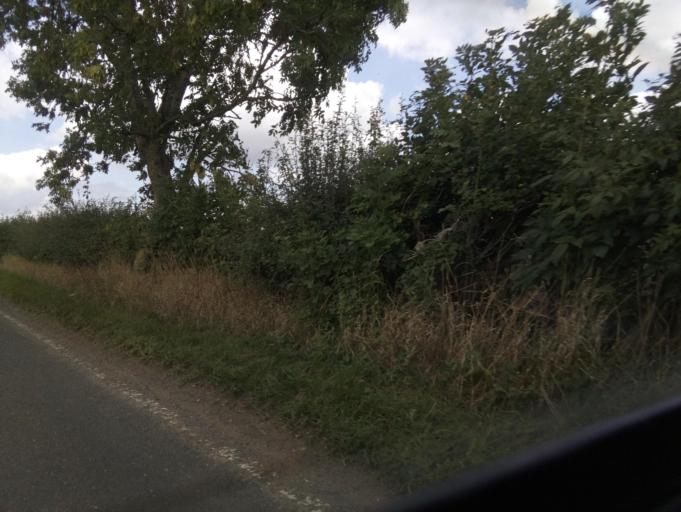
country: GB
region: England
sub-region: North Yorkshire
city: Catterick Garrison
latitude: 54.4284
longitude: -1.6814
